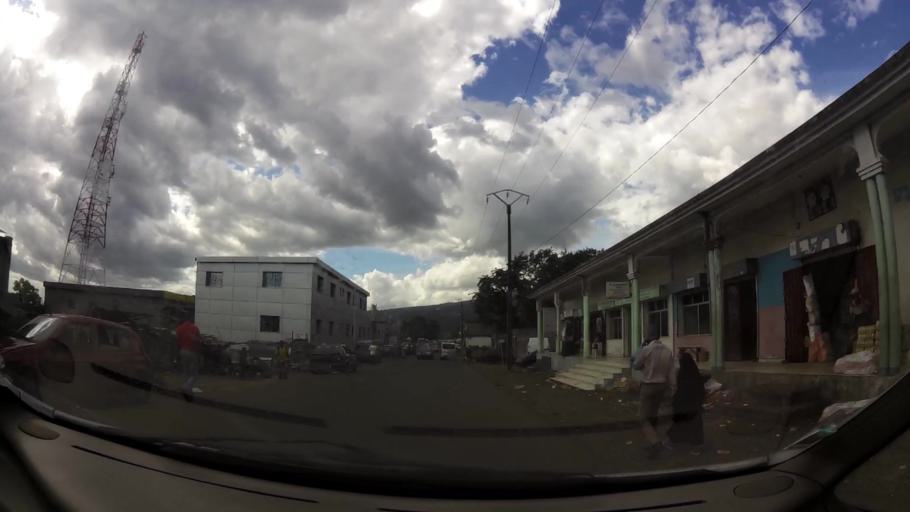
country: KM
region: Grande Comore
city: Tsidje
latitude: -11.6873
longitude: 43.2590
